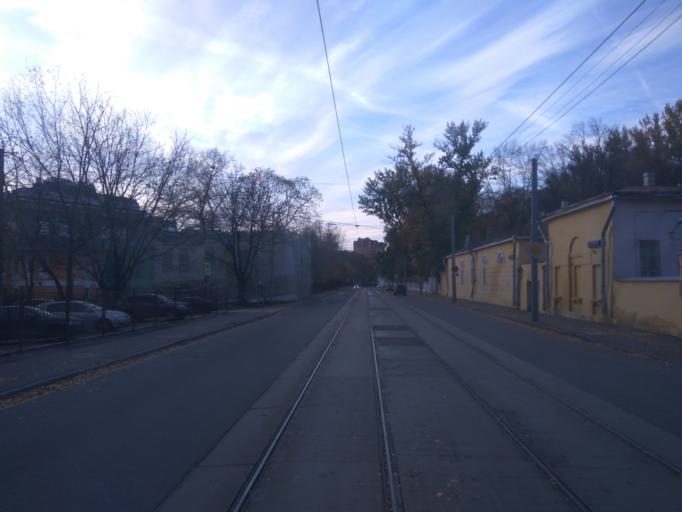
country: RU
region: Moscow
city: Mar'ina Roshcha
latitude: 55.7834
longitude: 37.6099
